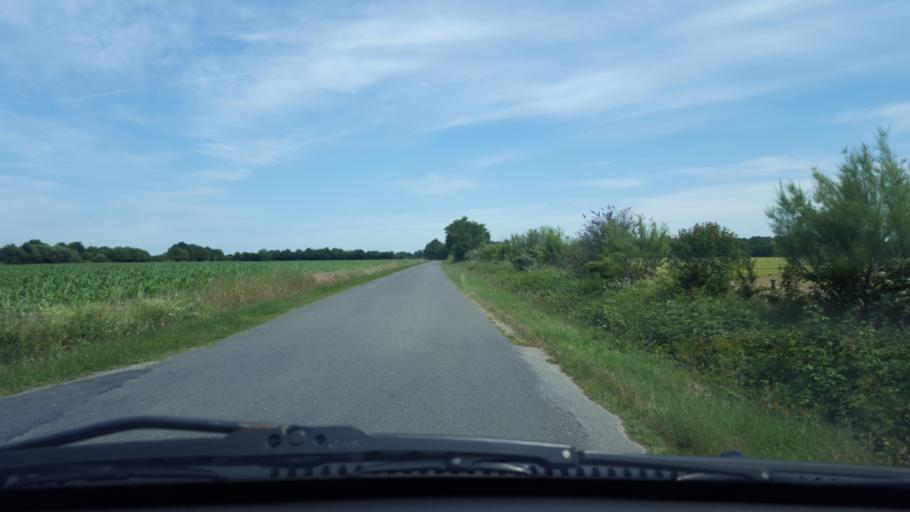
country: FR
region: Pays de la Loire
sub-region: Departement de la Loire-Atlantique
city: La Limouziniere
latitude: 47.0429
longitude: -1.5801
